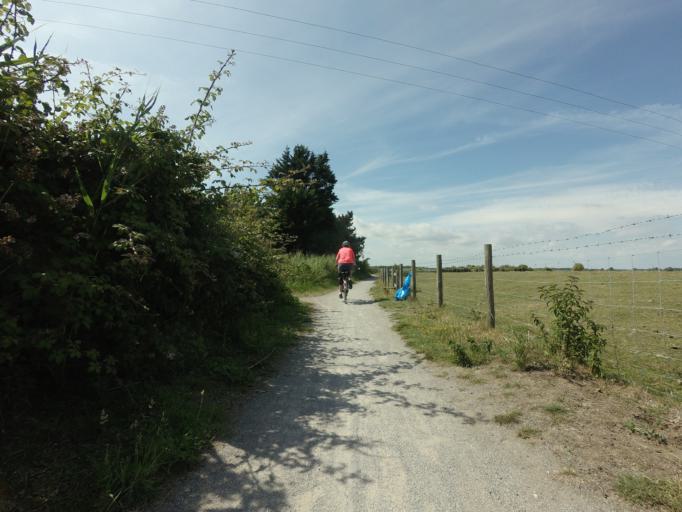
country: GB
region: England
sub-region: East Sussex
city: Rye
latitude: 50.9408
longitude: 0.7716
